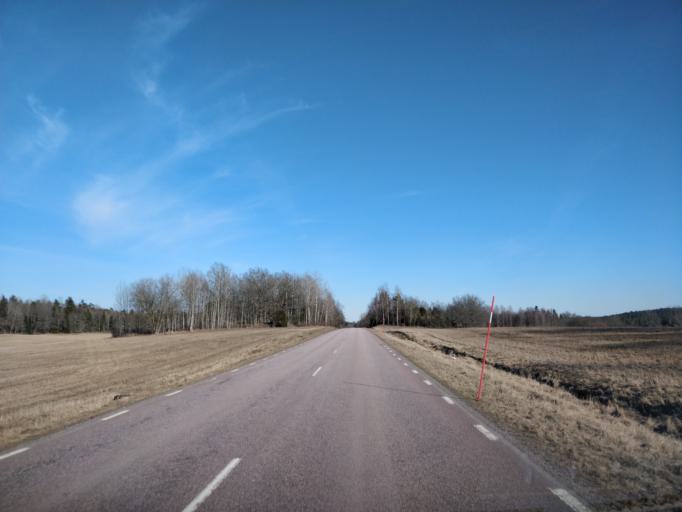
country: SE
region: Uppsala
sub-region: Enkopings Kommun
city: Orsundsbro
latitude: 59.7497
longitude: 17.2565
